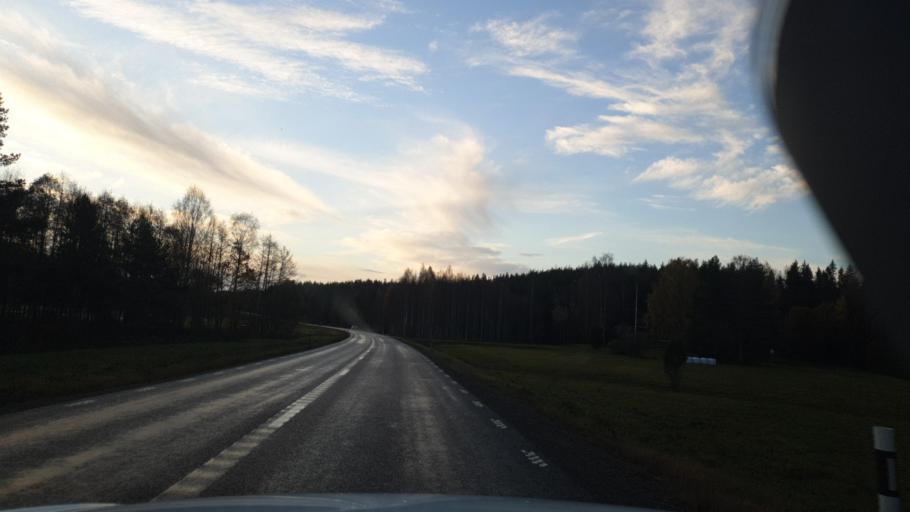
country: SE
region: Vaermland
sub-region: Arvika Kommun
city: Arvika
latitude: 59.5567
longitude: 12.7248
